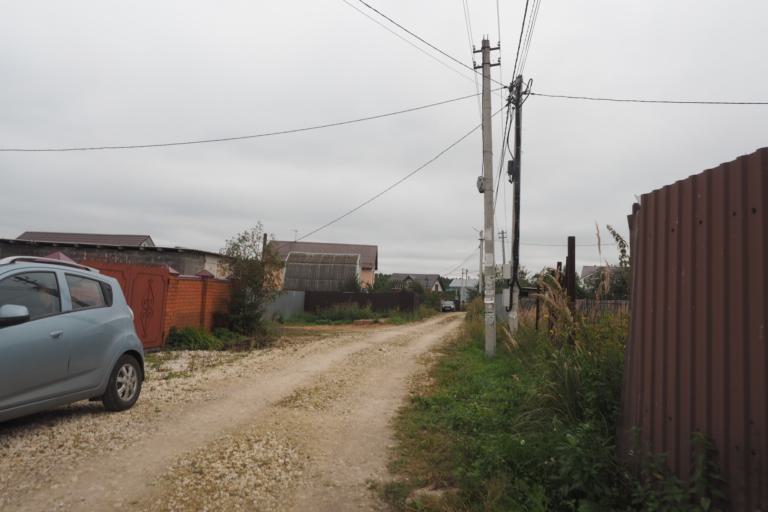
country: RU
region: Moskovskaya
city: Malyshevo
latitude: 55.5387
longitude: 38.3296
